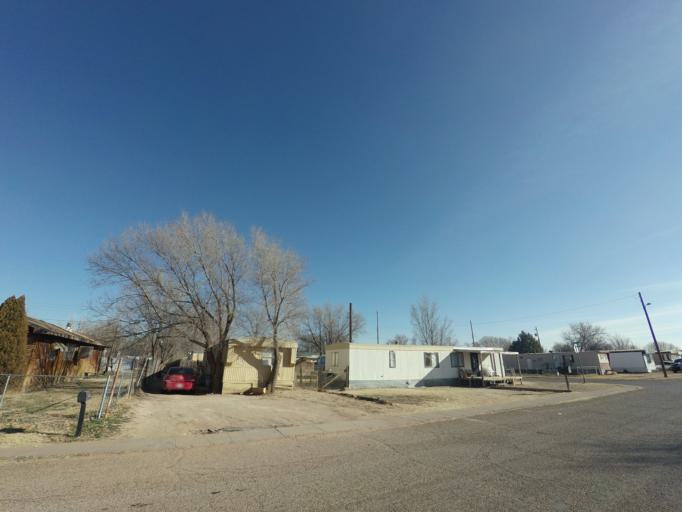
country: US
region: New Mexico
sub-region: Curry County
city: Clovis
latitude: 34.3881
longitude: -103.2009
